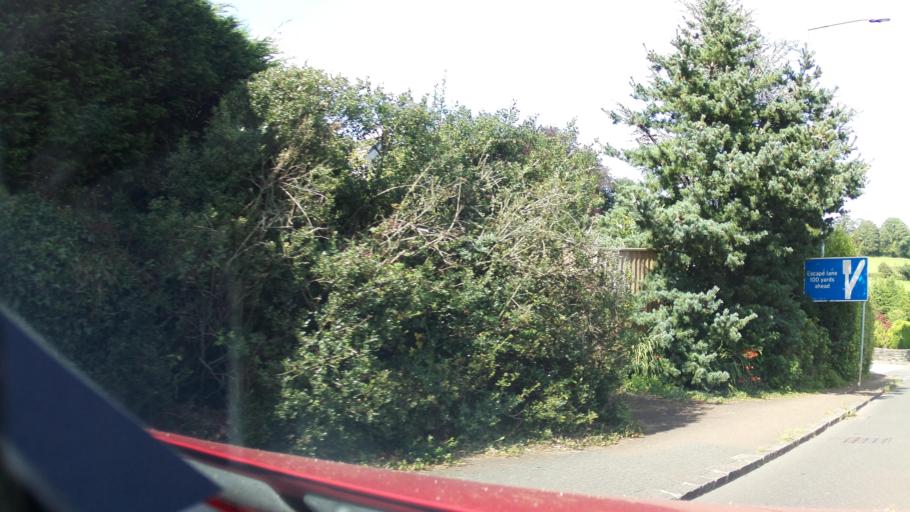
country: GB
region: England
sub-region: Cornwall
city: Gunnislake
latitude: 50.5179
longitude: -4.2189
